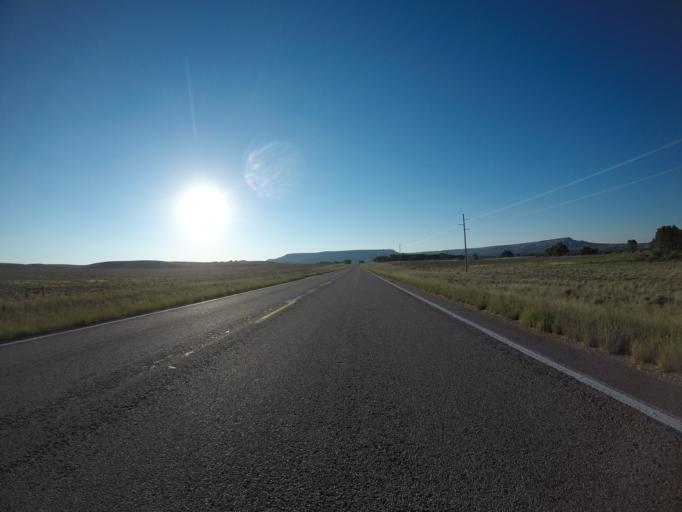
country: US
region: Wyoming
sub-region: Sublette County
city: Marbleton
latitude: 42.5710
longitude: -109.9660
